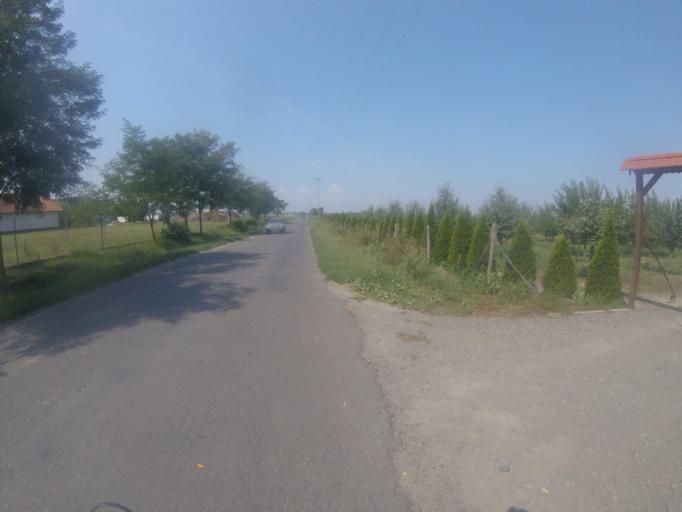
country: HU
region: Bacs-Kiskun
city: Ersekcsanad
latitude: 46.2550
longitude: 18.9556
